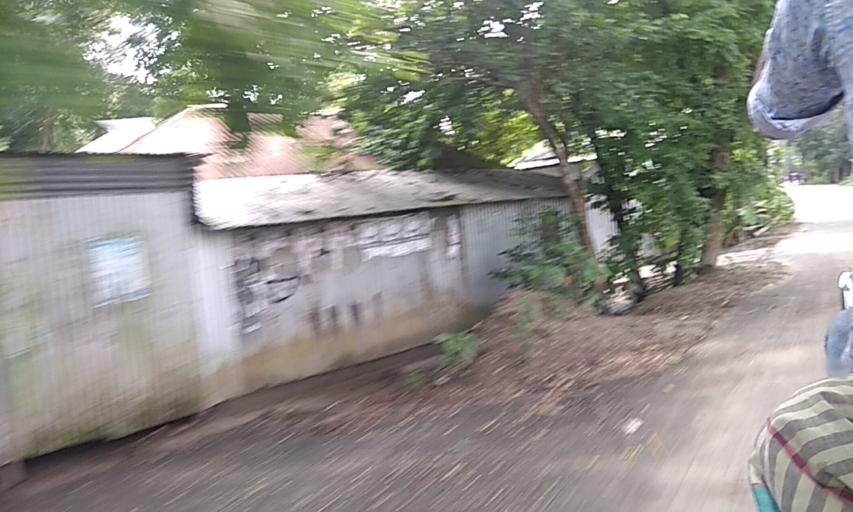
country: BD
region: Dhaka
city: Dohar
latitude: 23.4742
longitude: 90.0402
